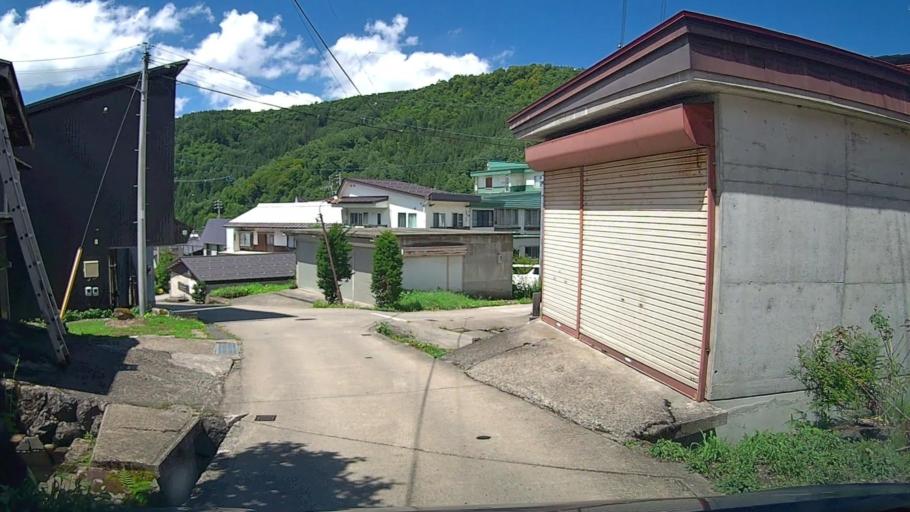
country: JP
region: Nagano
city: Iiyama
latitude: 36.9211
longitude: 138.4485
